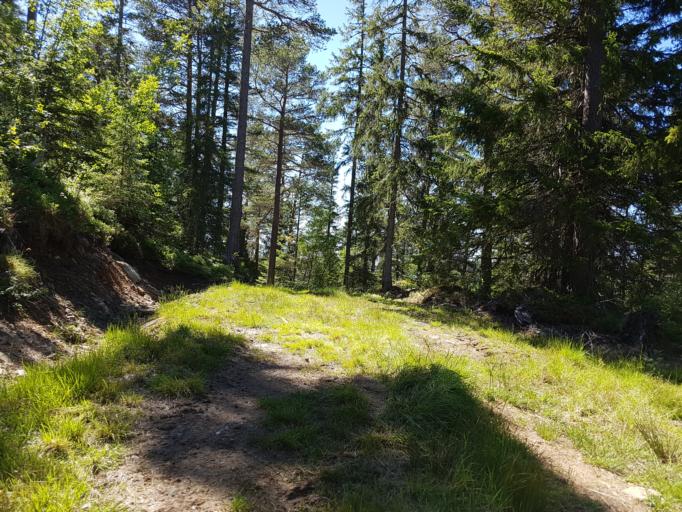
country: NO
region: Sor-Trondelag
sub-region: Melhus
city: Melhus
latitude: 63.4374
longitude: 10.2017
